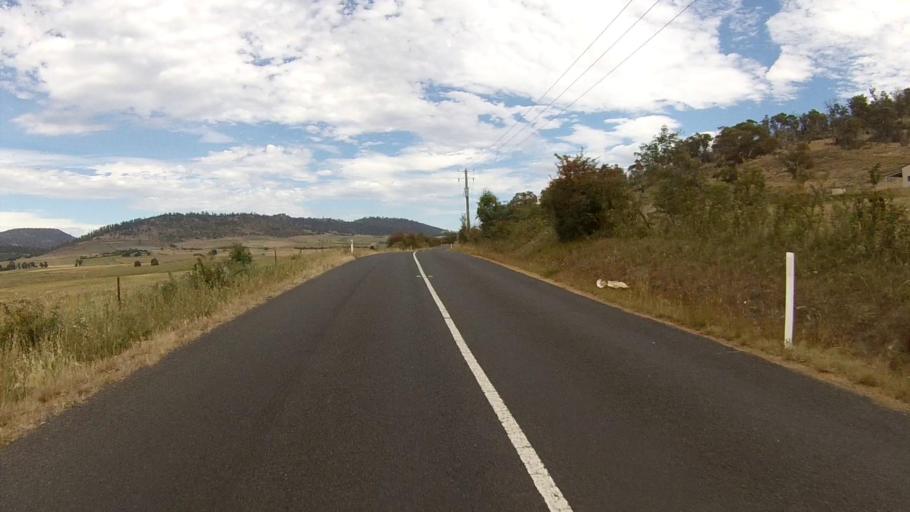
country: AU
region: Tasmania
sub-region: Clarence
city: Cambridge
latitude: -42.7367
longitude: 147.4140
